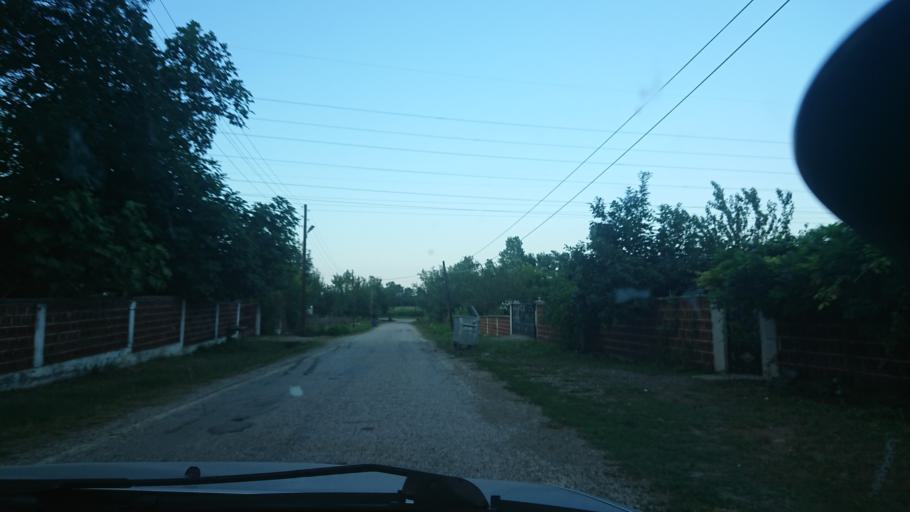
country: TR
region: Samsun
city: Dikbiyik
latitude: 41.1777
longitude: 36.5456
